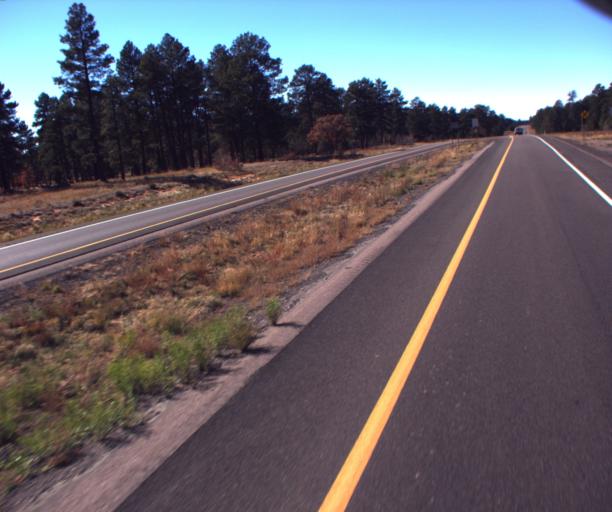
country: US
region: Arizona
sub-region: Apache County
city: Saint Michaels
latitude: 35.6813
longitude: -109.2168
